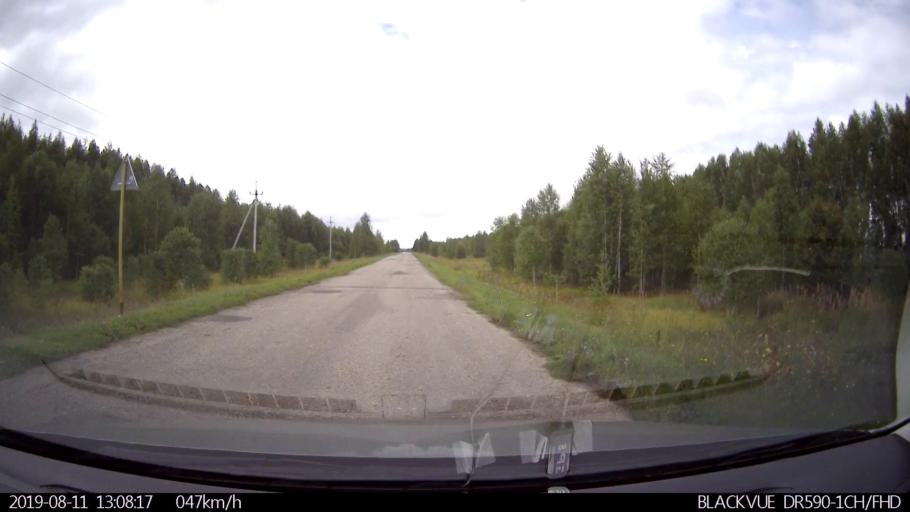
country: RU
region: Ulyanovsk
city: Ignatovka
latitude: 53.8588
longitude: 47.6359
